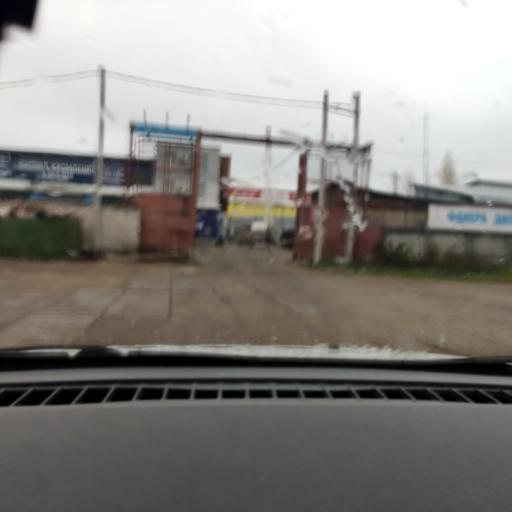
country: RU
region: Perm
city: Kondratovo
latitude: 57.9445
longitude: 56.1510
